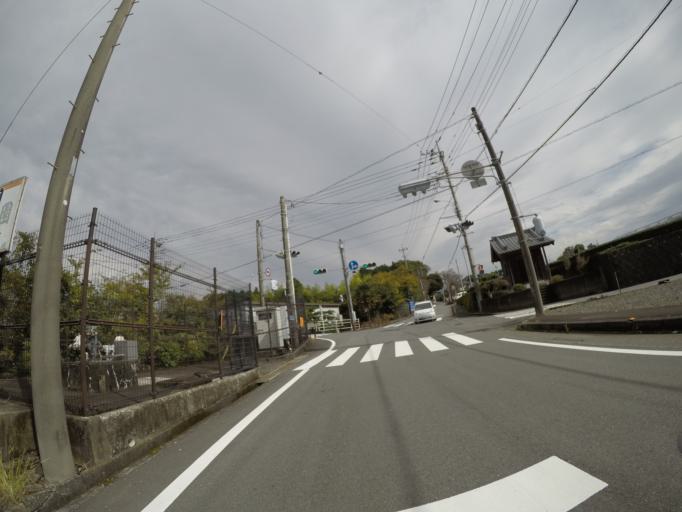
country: JP
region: Shizuoka
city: Fuji
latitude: 35.2087
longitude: 138.6716
